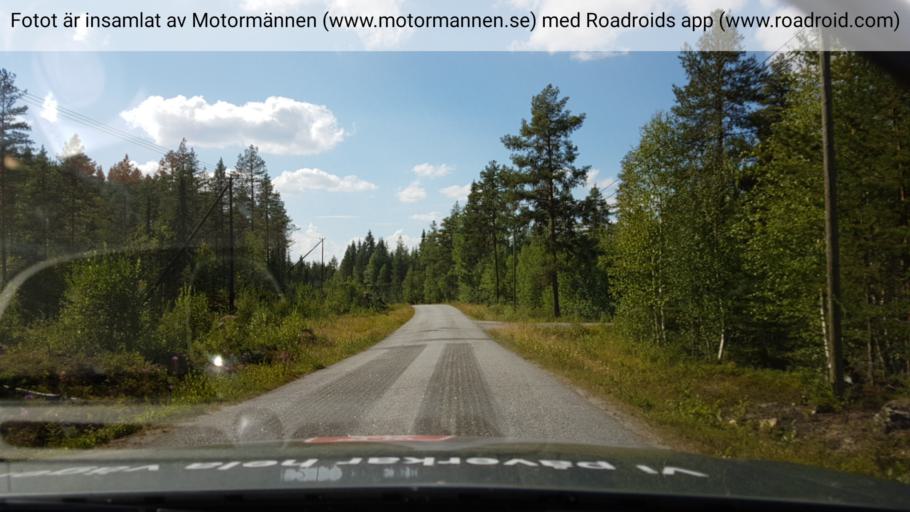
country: SE
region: Vaesterbotten
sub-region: Dorotea Kommun
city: Dorotea
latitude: 64.1074
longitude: 16.3539
